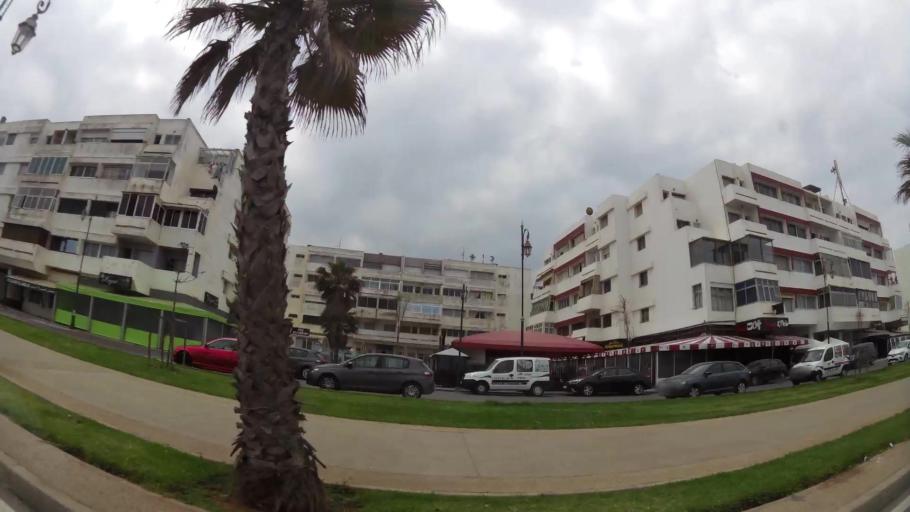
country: MA
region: Rabat-Sale-Zemmour-Zaer
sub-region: Rabat
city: Rabat
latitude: 33.9931
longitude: -6.8822
